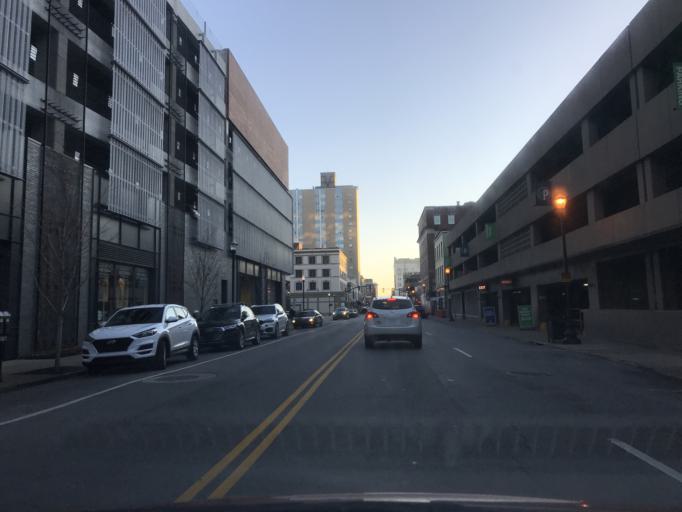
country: US
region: Kentucky
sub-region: Jefferson County
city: Louisville
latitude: 38.2522
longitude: -85.7557
